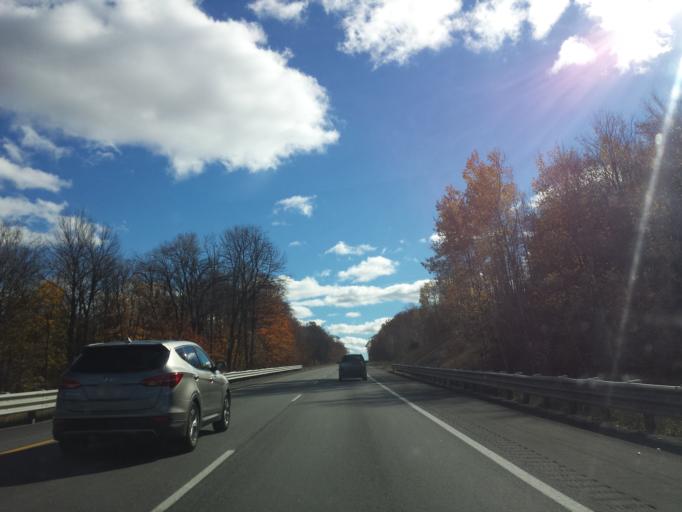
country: US
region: Michigan
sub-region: Cheboygan County
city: Indian River
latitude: 45.3403
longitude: -84.6082
